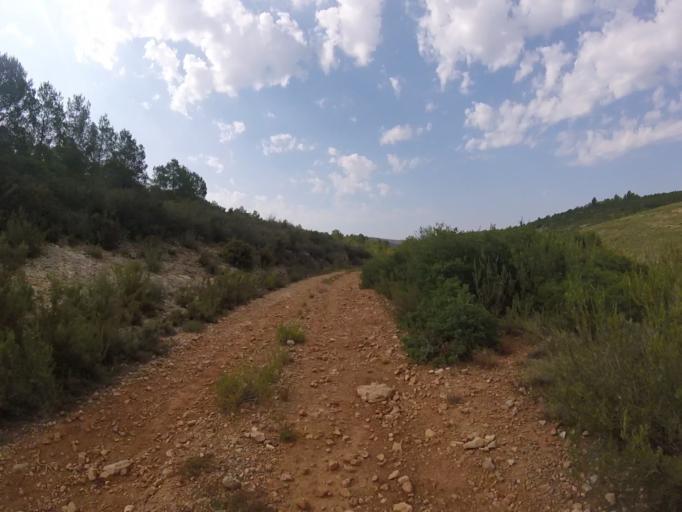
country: ES
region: Valencia
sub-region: Provincia de Castello
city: Alcala de Xivert
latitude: 40.3466
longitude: 0.1984
